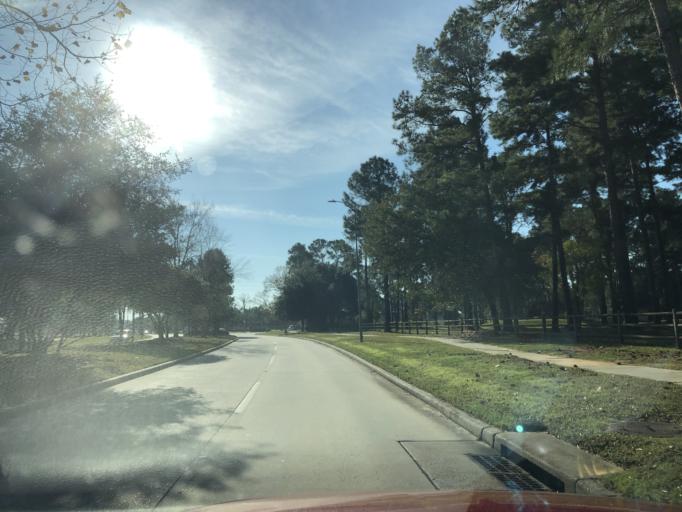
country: US
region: Texas
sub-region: Harris County
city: Tomball
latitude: 30.0383
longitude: -95.5624
